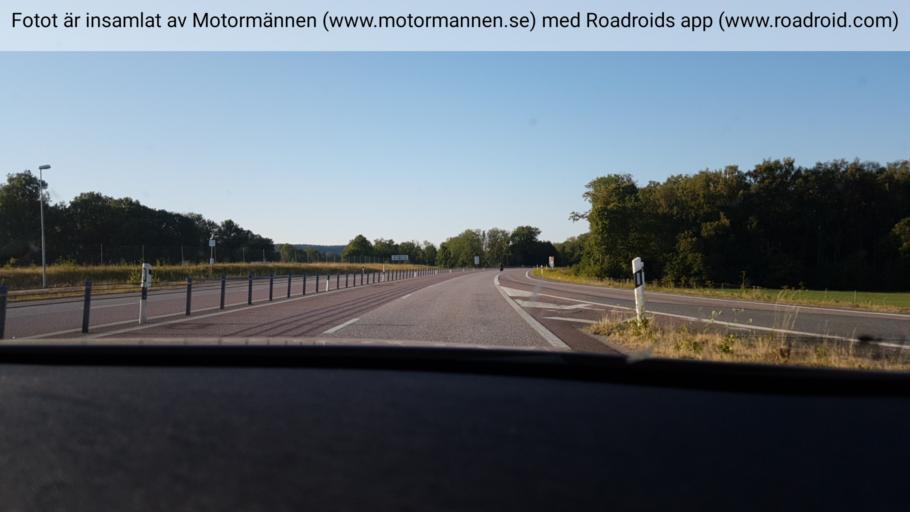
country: SE
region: Vaestra Goetaland
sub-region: Skovde Kommun
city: Skultorp
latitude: 58.3110
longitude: 13.8099
